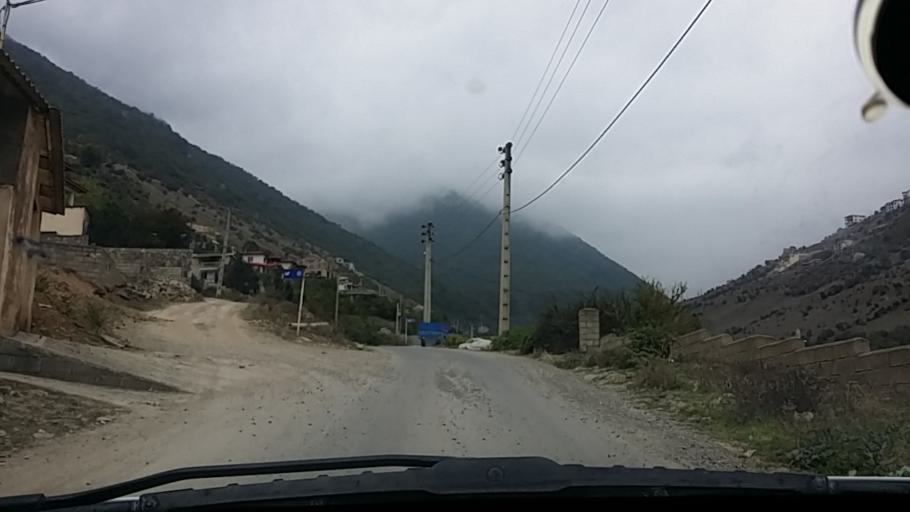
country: IR
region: Mazandaran
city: `Abbasabad
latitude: 36.4751
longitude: 51.1401
